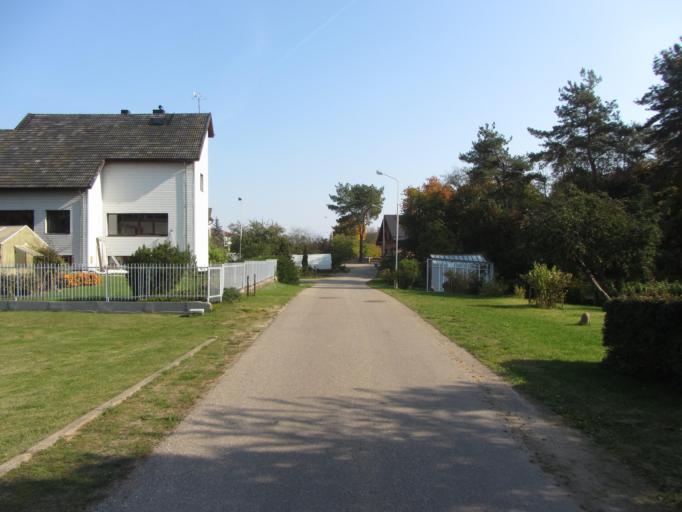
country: LT
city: Trakai
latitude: 54.6231
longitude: 24.9200
